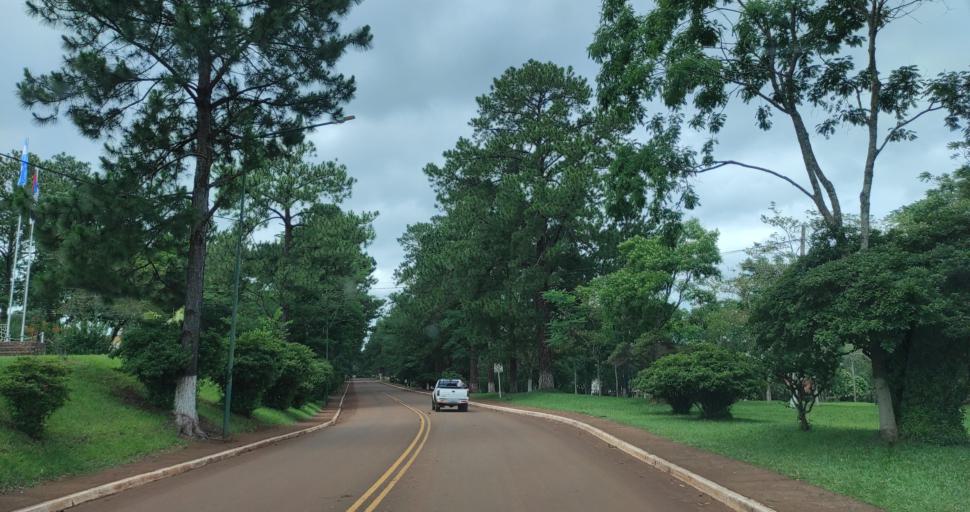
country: AR
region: Misiones
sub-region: Departamento de Veinticinco de Mayo
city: Veinticinco de Mayo
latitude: -27.3794
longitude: -54.7453
